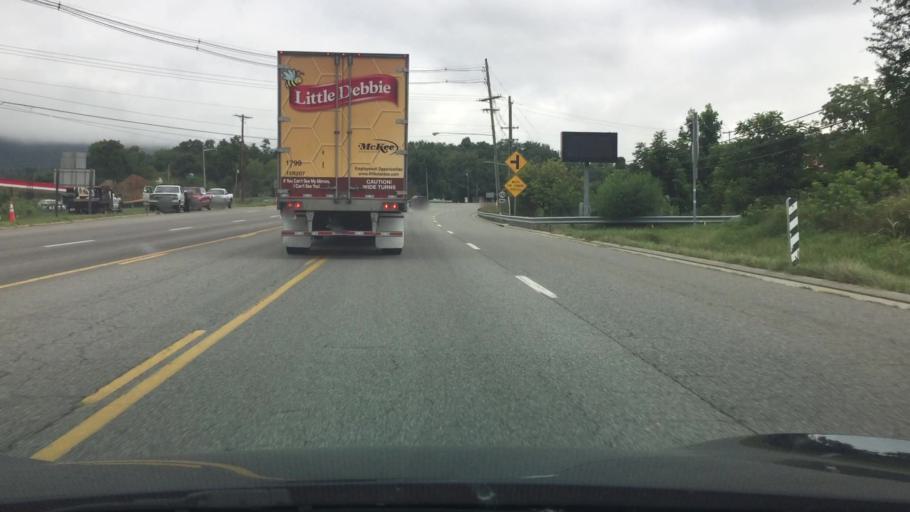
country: US
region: Virginia
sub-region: Montgomery County
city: Shawsville
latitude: 37.2533
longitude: -80.1738
